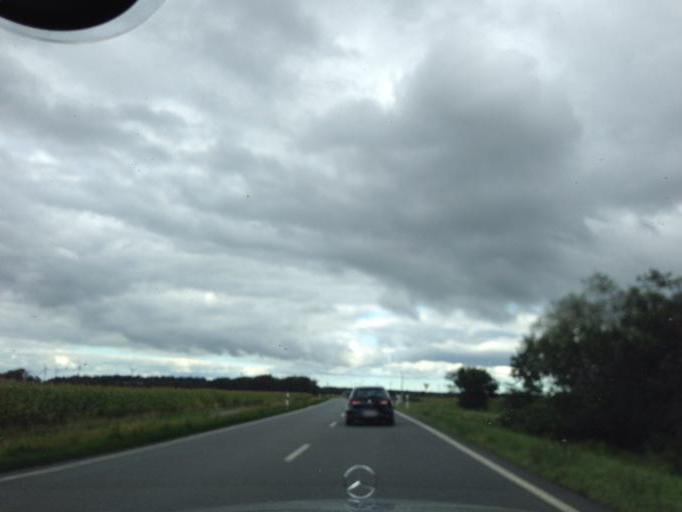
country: DE
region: Schleswig-Holstein
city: Horup
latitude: 54.7460
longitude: 9.0754
